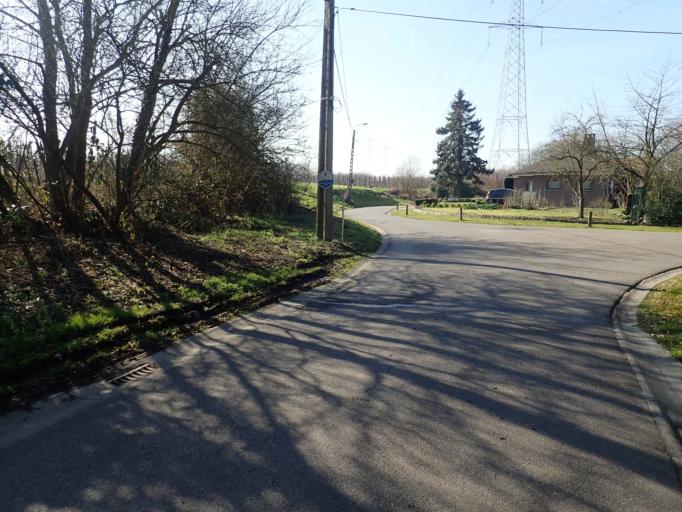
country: BE
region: Flanders
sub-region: Provincie Antwerpen
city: Bornem
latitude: 51.1272
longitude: 4.2488
